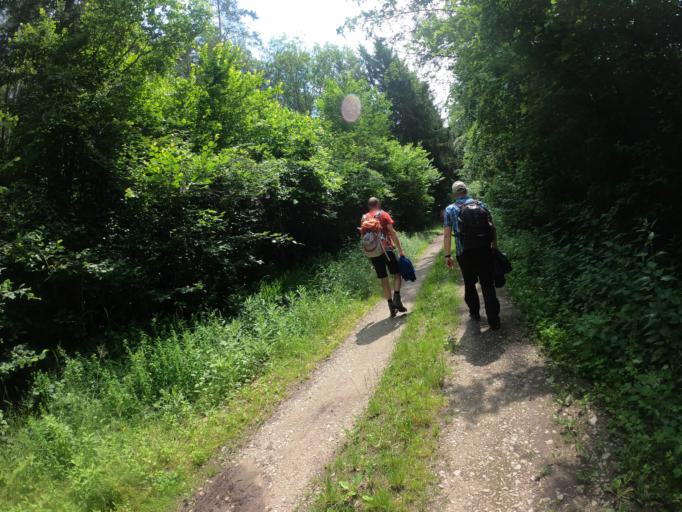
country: DE
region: Bavaria
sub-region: Upper Franconia
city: Poxdorf
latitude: 49.9233
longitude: 11.0718
